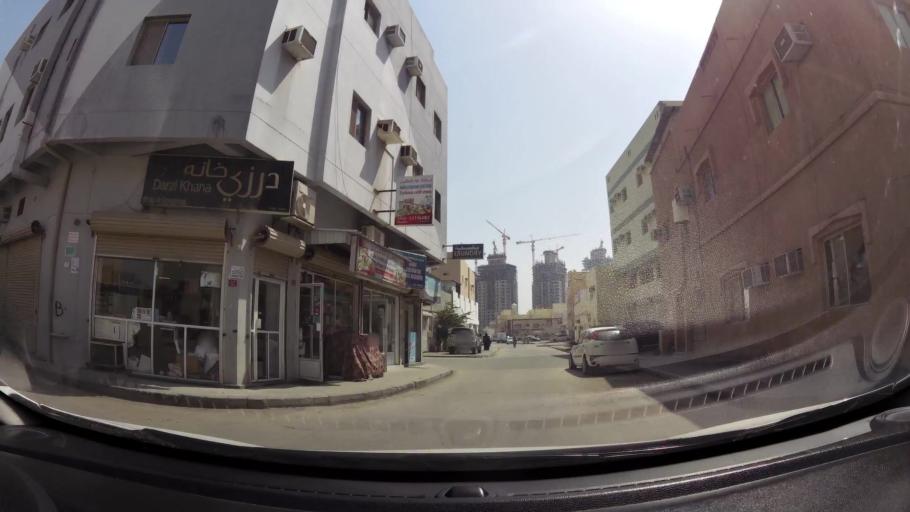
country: BH
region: Manama
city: Jidd Hafs
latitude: 26.2086
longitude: 50.4507
